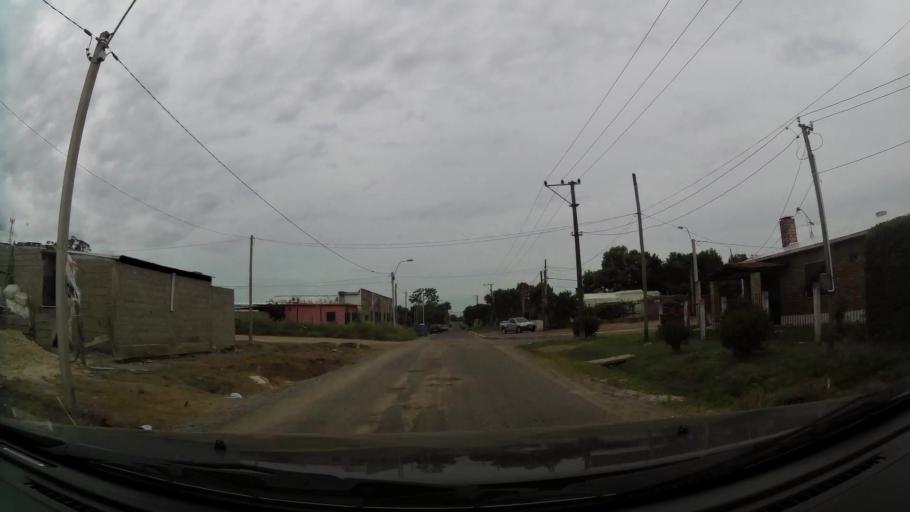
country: UY
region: Canelones
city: Las Piedras
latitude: -34.7212
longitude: -56.2028
